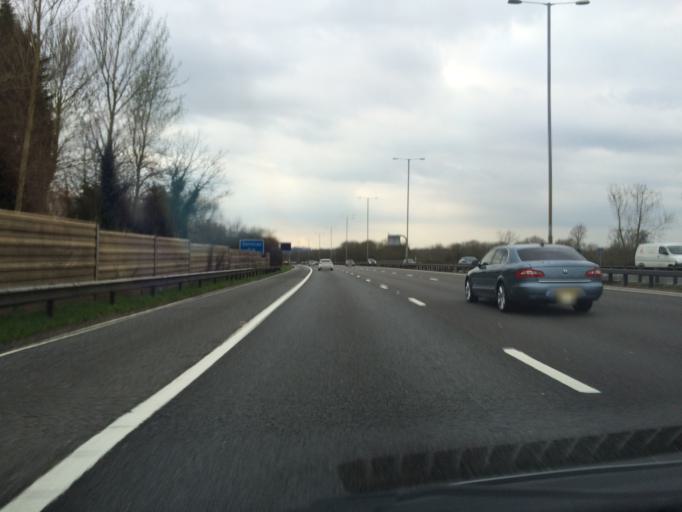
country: GB
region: England
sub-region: Wokingham
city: Winnersh
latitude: 51.4246
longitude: -0.8877
